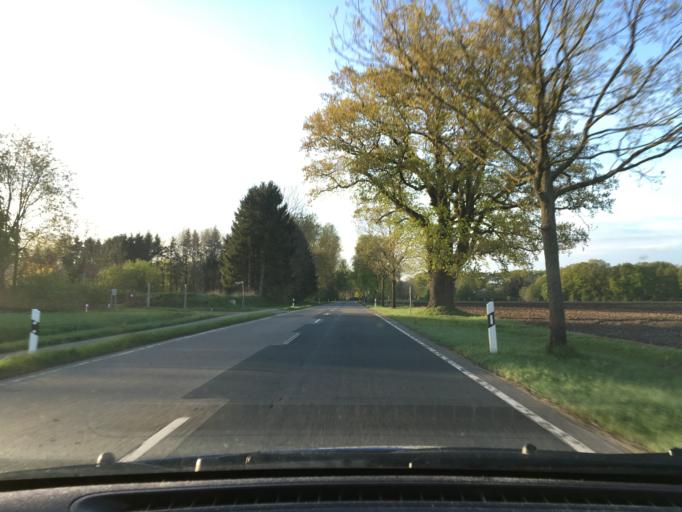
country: DE
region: Lower Saxony
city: Bispingen
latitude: 53.0233
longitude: 9.9986
